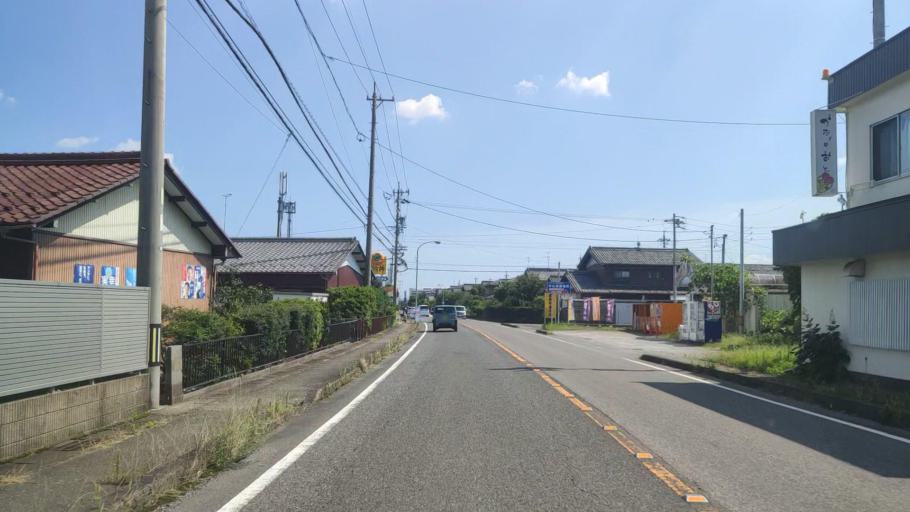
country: JP
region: Gifu
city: Godo
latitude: 35.4701
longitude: 136.6752
